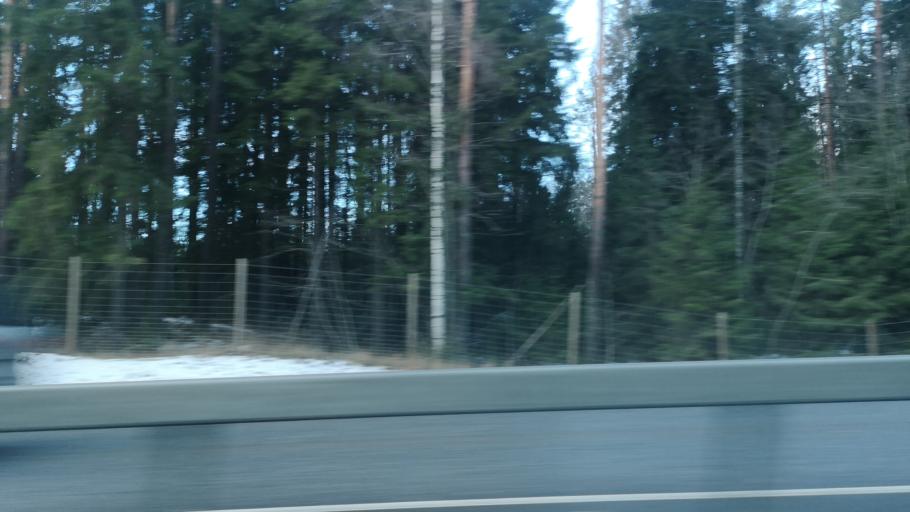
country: FI
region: Southern Savonia
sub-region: Mikkeli
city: Maentyharju
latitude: 61.5006
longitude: 26.7907
